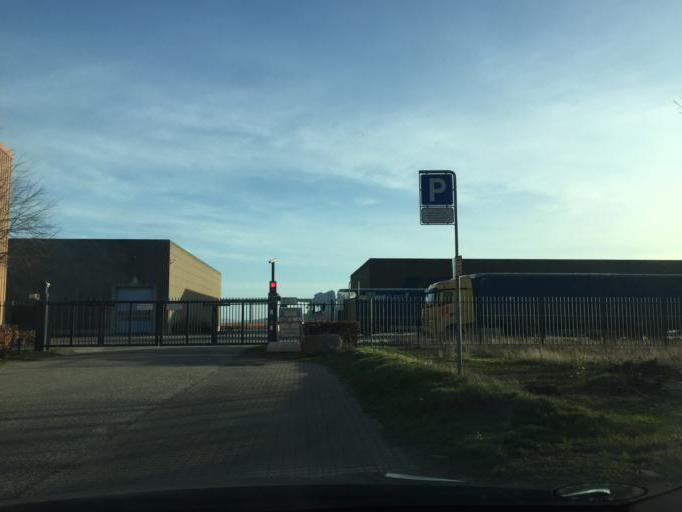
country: DK
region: South Denmark
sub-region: Vejle Kommune
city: Vejle
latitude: 55.7031
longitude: 9.5564
